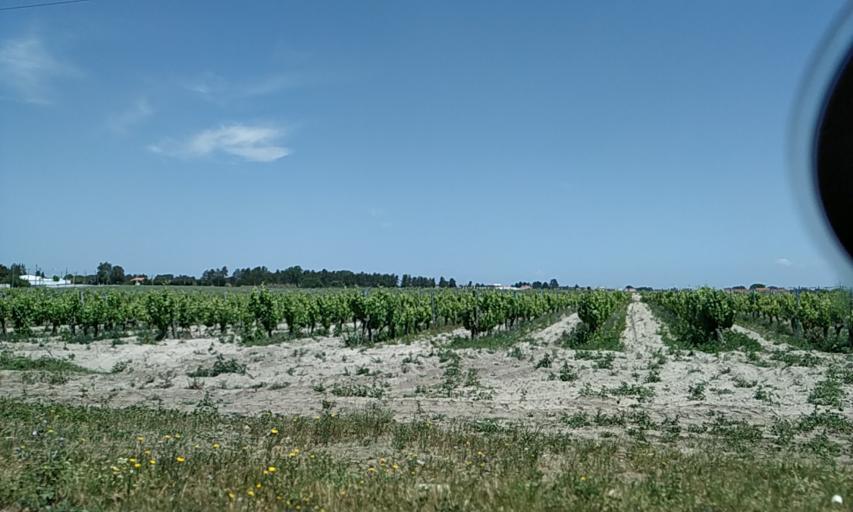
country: PT
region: Setubal
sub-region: Palmela
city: Pinhal Novo
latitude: 38.6379
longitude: -8.7421
